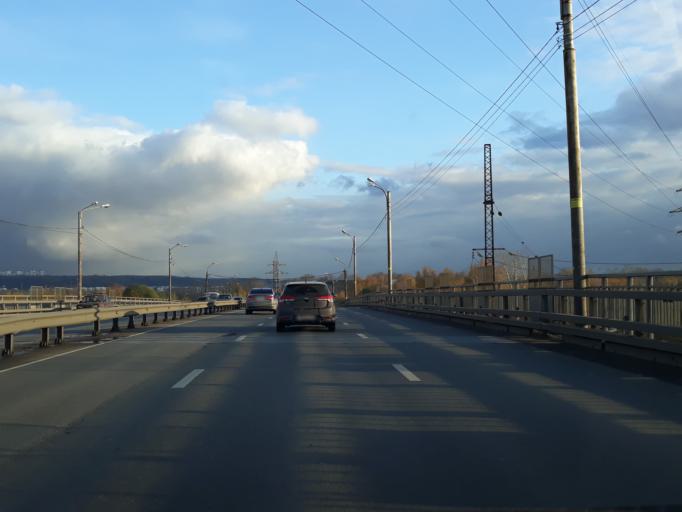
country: RU
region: Nizjnij Novgorod
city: Nizhniy Novgorod
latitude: 56.3065
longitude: 43.9050
